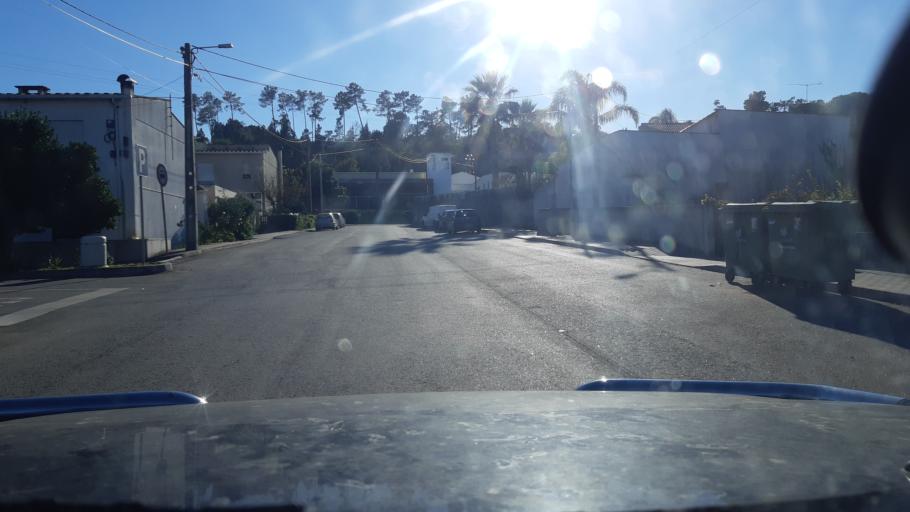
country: PT
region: Aveiro
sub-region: Agueda
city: Agueda
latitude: 40.5633
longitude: -8.4439
